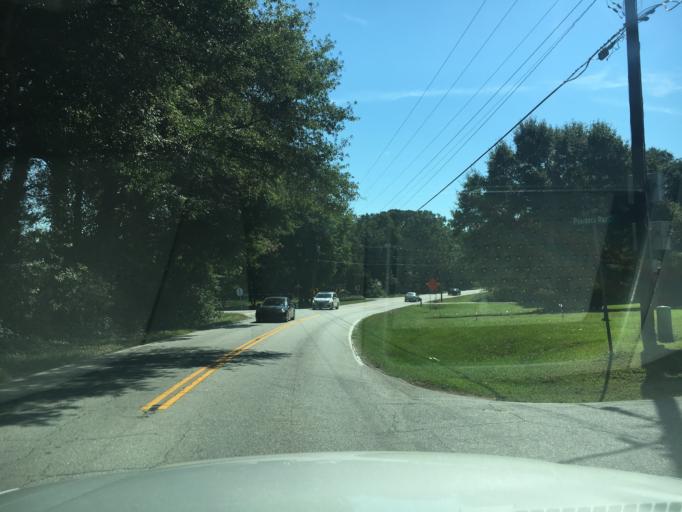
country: US
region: South Carolina
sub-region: Greenville County
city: Mauldin
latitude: 34.8432
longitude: -82.2937
